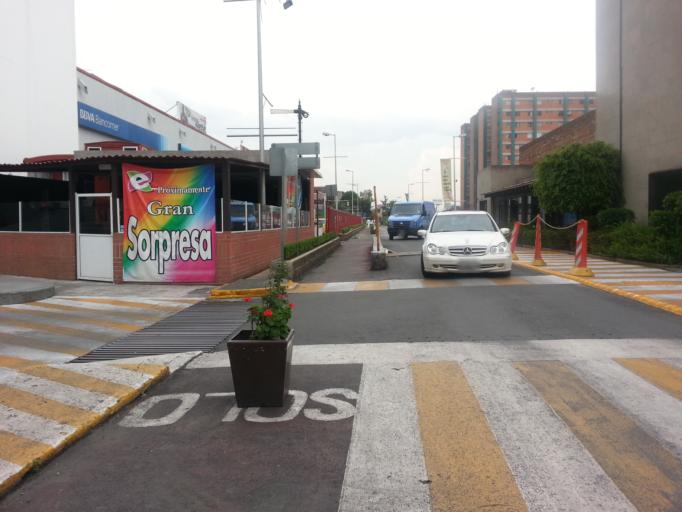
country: MX
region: Mexico City
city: Colonia del Valle
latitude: 19.3883
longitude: -99.1911
